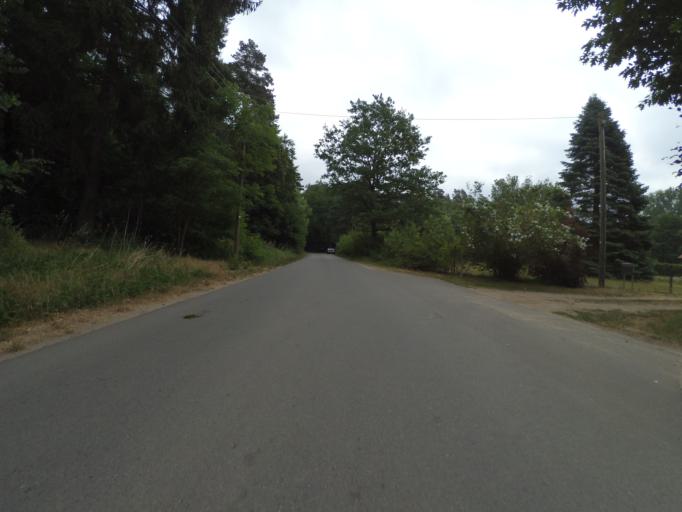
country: DE
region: Mecklenburg-Vorpommern
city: Krakow am See
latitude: 53.6688
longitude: 12.2993
